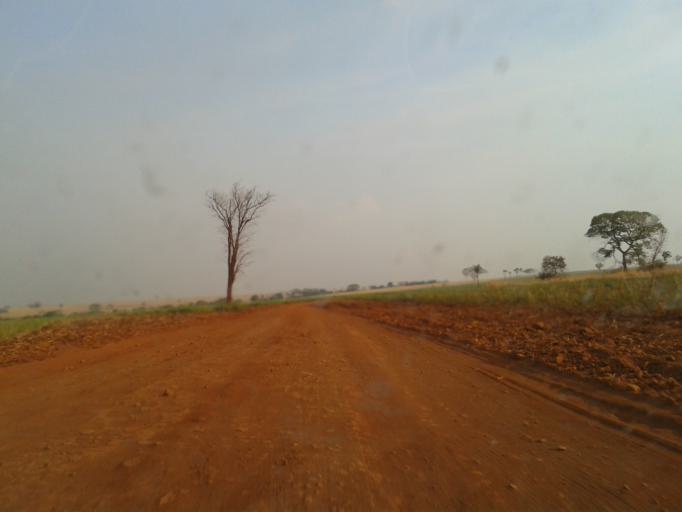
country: BR
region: Minas Gerais
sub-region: Capinopolis
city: Capinopolis
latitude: -18.7229
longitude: -49.6842
